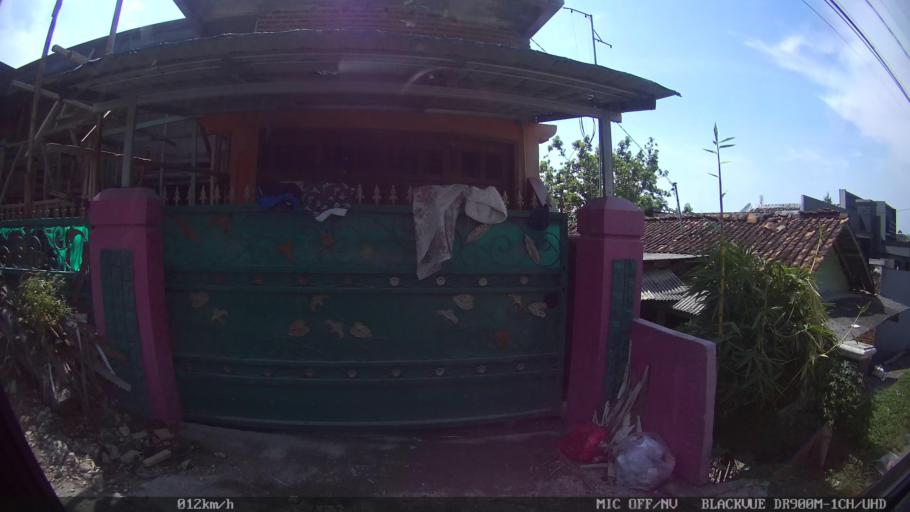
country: ID
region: Lampung
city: Kedaton
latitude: -5.3997
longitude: 105.2508
